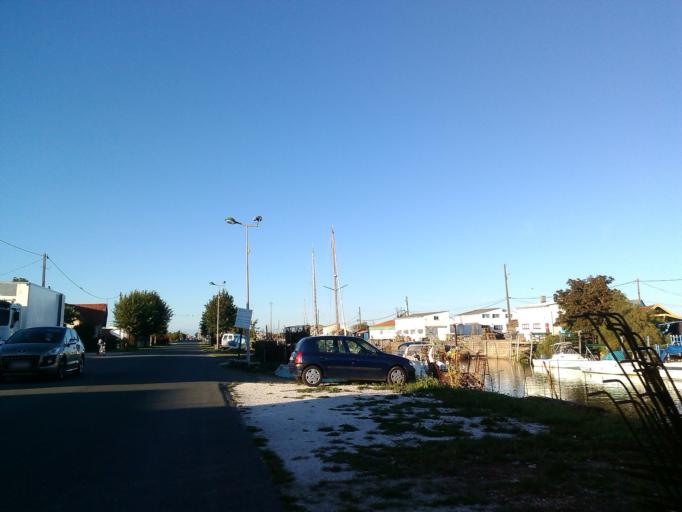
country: FR
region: Poitou-Charentes
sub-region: Departement de la Charente-Maritime
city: La Tremblade
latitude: 45.7699
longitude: -1.1336
